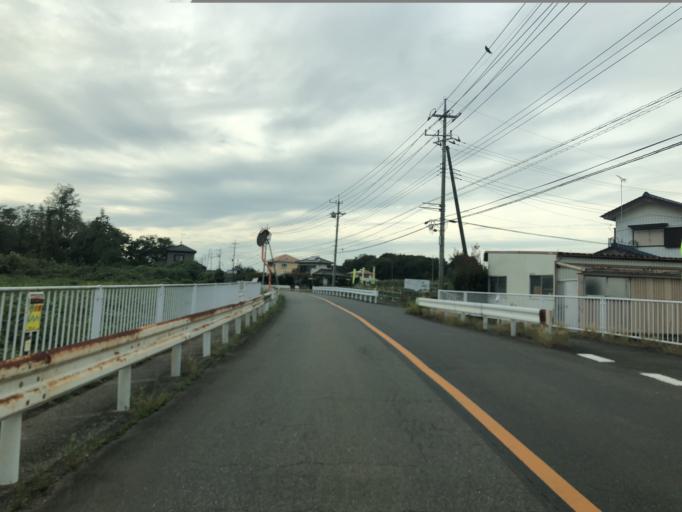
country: JP
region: Saitama
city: Fukiage-fujimi
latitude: 36.0610
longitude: 139.3987
